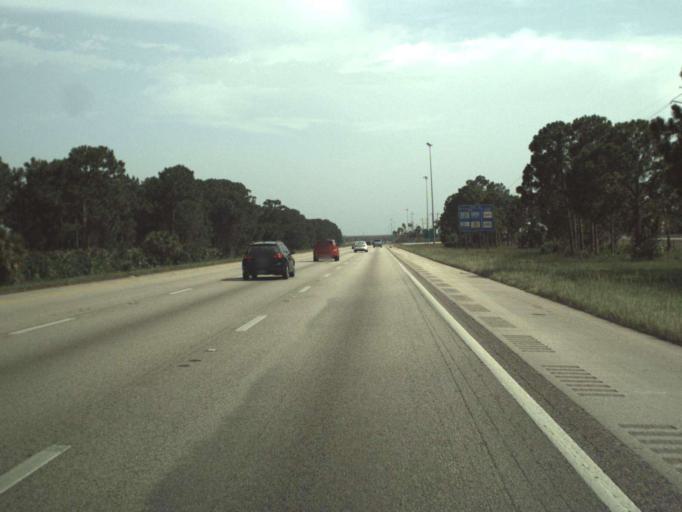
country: US
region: Florida
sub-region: Saint Lucie County
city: River Park
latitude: 27.3207
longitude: -80.4145
